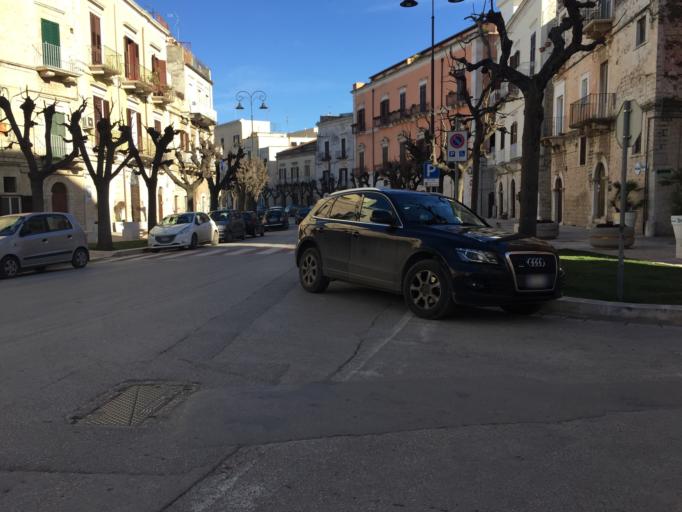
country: IT
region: Apulia
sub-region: Provincia di Bari
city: Terlizzi
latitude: 41.1274
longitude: 16.5385
